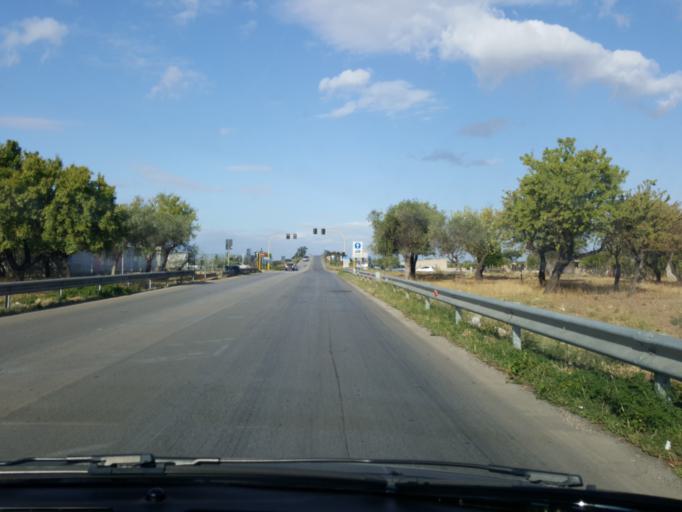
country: IT
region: Apulia
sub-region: Provincia di Bari
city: Triggiano
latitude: 41.0566
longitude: 16.9234
